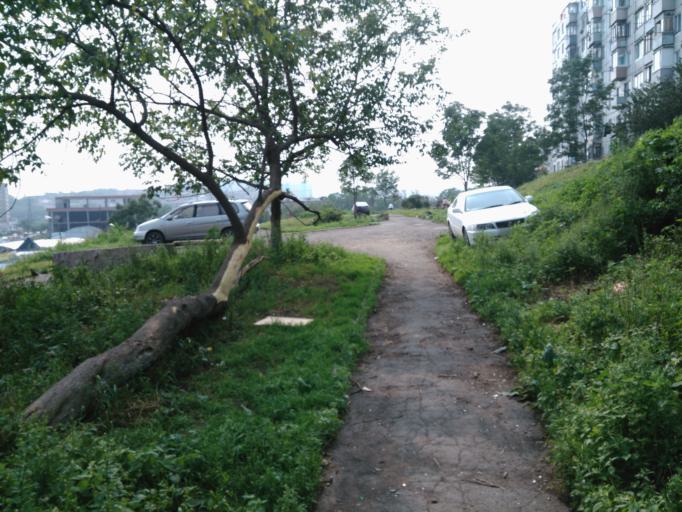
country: RU
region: Primorskiy
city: Vladivostok
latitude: 43.0927
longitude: 131.9728
